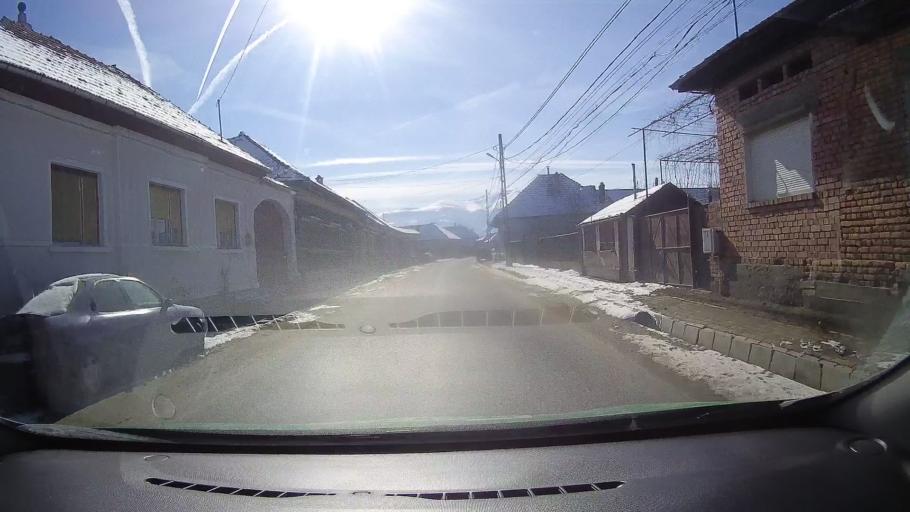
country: RO
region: Brasov
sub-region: Comuna Sambata de Sus
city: Sambata de Sus
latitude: 45.7598
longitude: 24.8304
